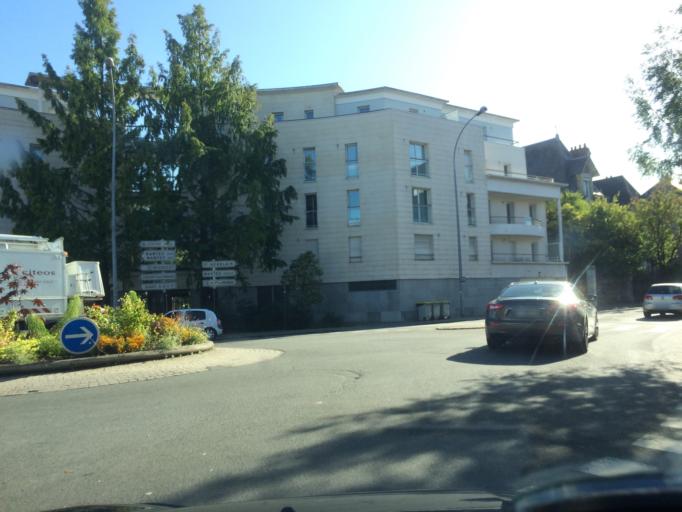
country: FR
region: Pays de la Loire
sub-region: Departement de la Loire-Atlantique
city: Nantes
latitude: 47.2344
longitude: -1.5635
